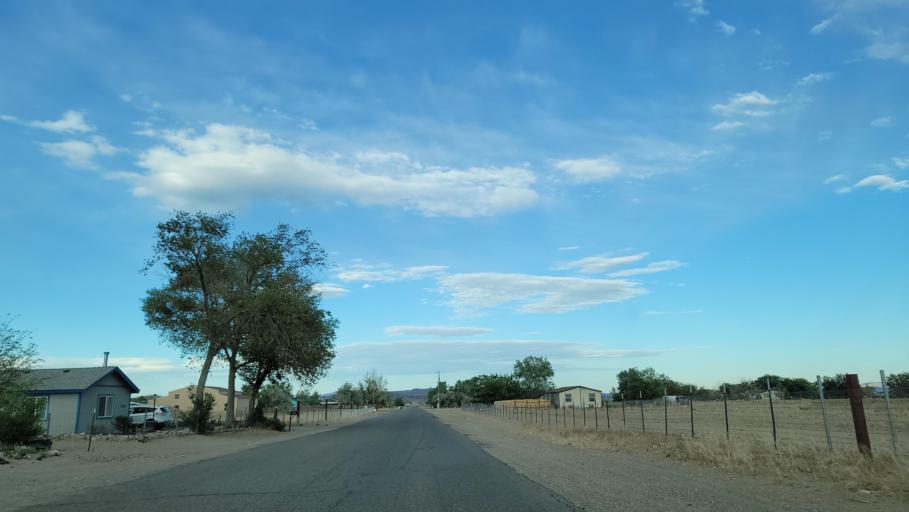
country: US
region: Nevada
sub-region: Lyon County
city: Silver Springs
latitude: 39.3899
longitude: -119.2397
